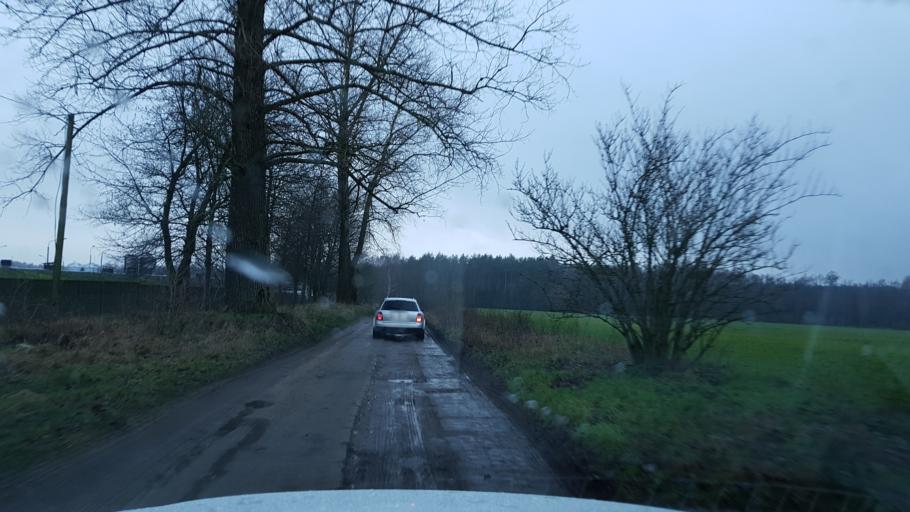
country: PL
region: West Pomeranian Voivodeship
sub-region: Powiat goleniowski
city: Osina
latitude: 53.5817
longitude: 15.0704
